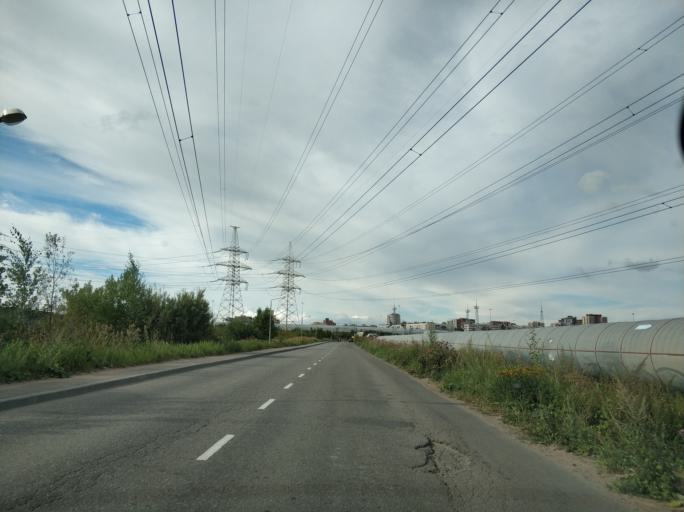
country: RU
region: Leningrad
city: Murino
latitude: 60.0473
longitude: 30.4369
